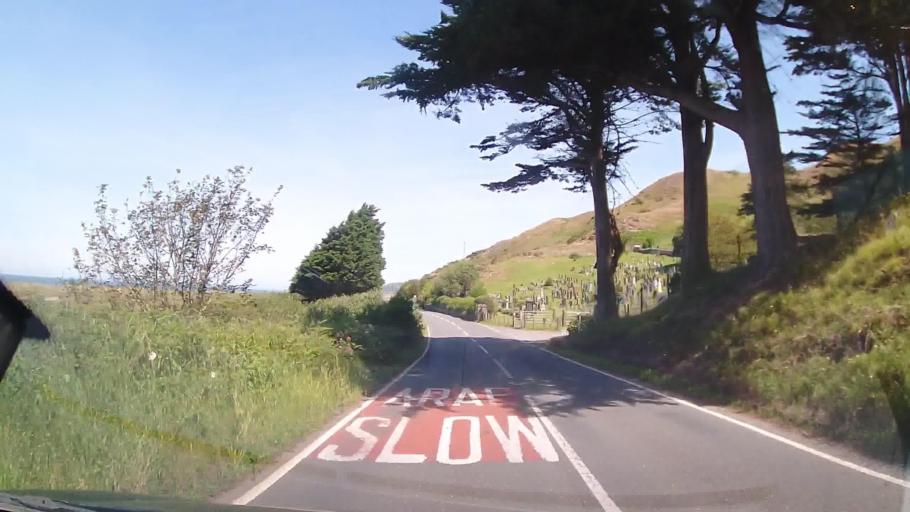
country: GB
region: Wales
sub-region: Gwynedd
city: Tywyn
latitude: 52.5532
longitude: -4.0704
